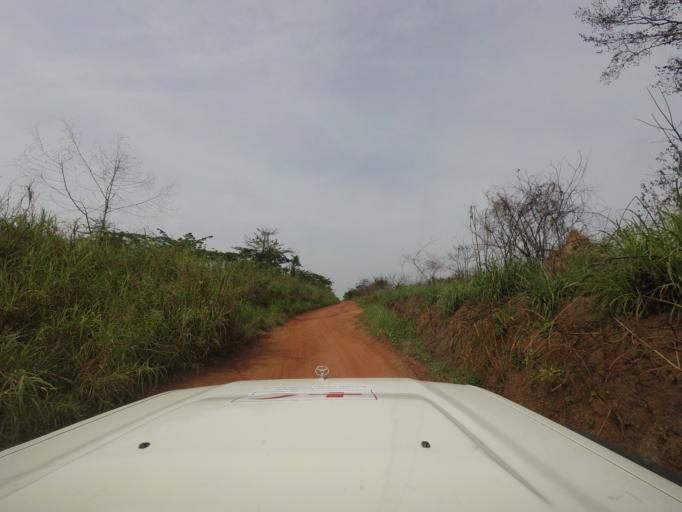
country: GN
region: Nzerekore
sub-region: Macenta
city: Macenta
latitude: 8.5184
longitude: -9.5195
